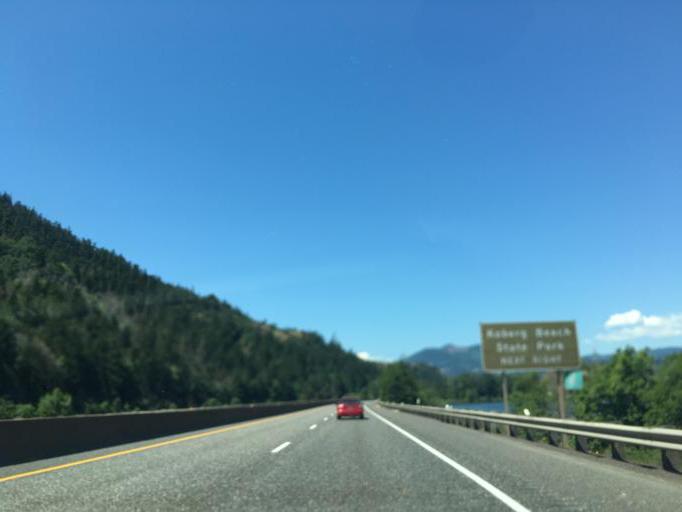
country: US
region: Washington
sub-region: Klickitat County
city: White Salmon
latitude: 45.6984
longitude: -121.4650
